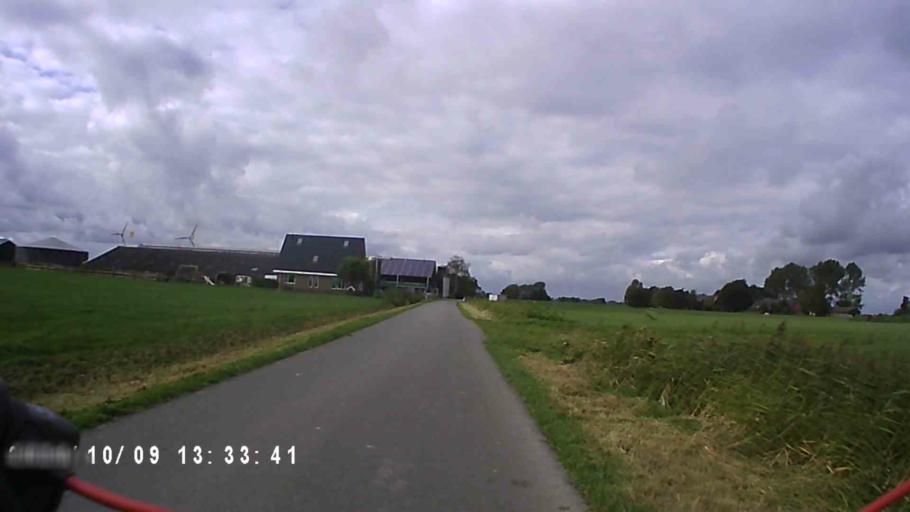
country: NL
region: Groningen
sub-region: Gemeente Zuidhorn
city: Aduard
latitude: 53.2891
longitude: 6.4717
